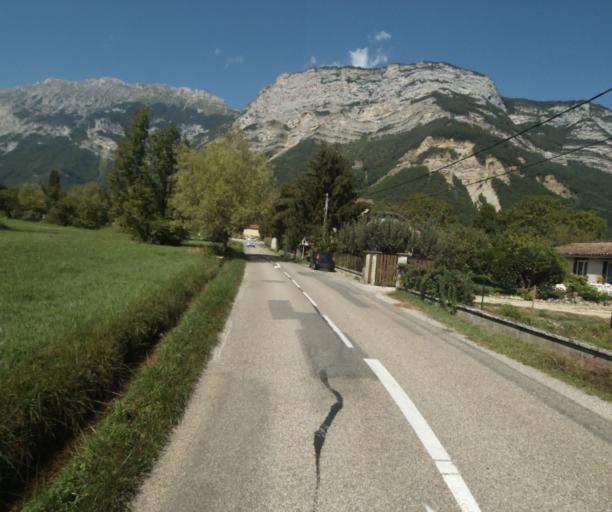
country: FR
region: Rhone-Alpes
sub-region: Departement de l'Isere
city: Allieres-et-Risset
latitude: 45.0799
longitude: 5.6652
